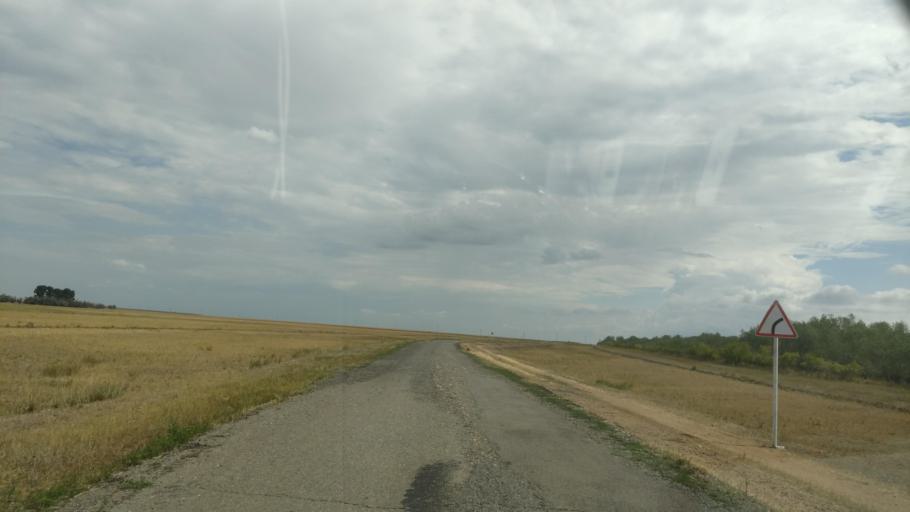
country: KZ
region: Pavlodar
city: Pavlodar
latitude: 52.6434
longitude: 77.0320
